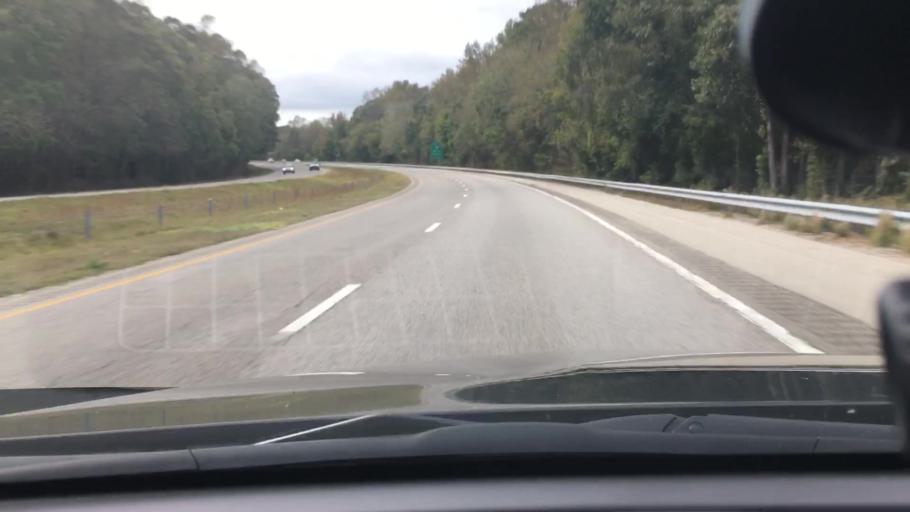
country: US
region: North Carolina
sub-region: Wilson County
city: Wilson
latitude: 35.6802
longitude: -77.8425
